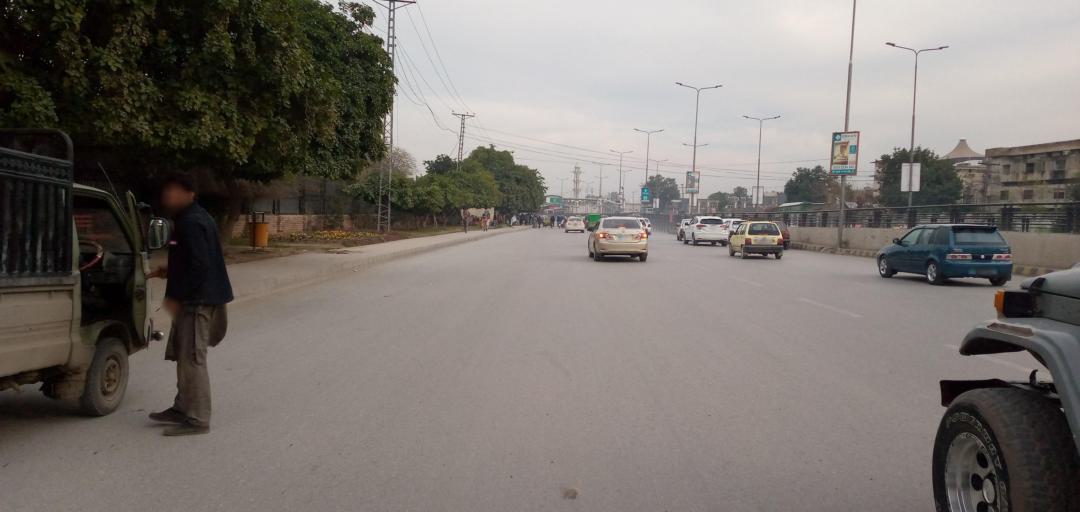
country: PK
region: Khyber Pakhtunkhwa
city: Peshawar
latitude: 33.9981
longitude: 71.4833
